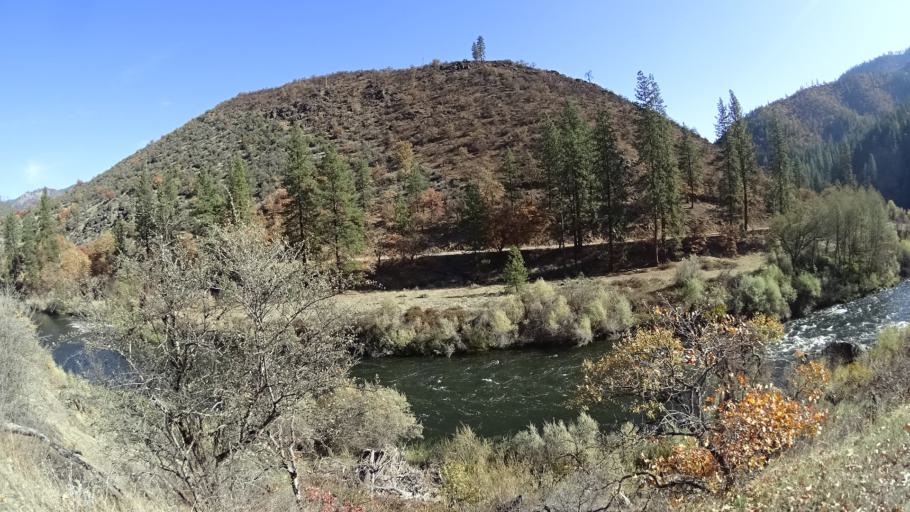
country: US
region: California
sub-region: Siskiyou County
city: Yreka
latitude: 41.8645
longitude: -122.7375
